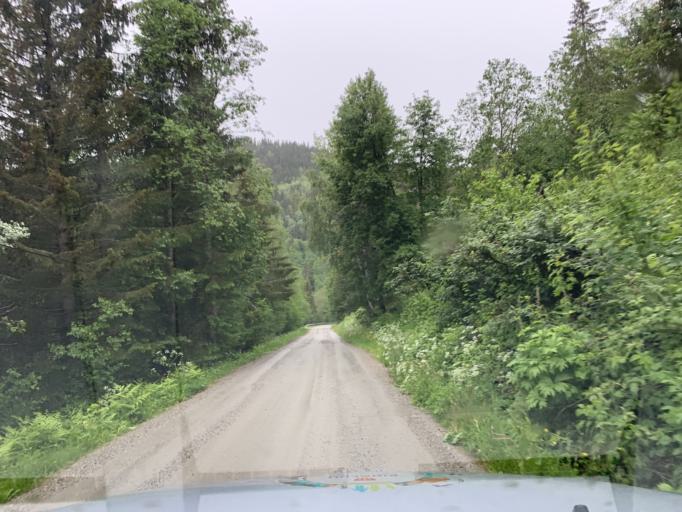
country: NO
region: Oppland
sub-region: Oyer
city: Tretten
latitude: 61.3911
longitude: 10.2766
